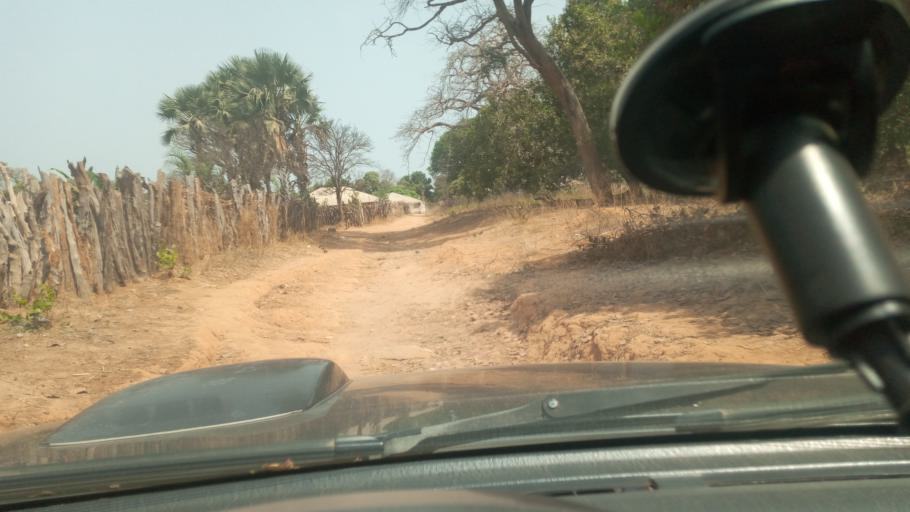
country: SN
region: Sedhiou
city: Sedhiou
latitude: 12.4406
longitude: -15.6157
